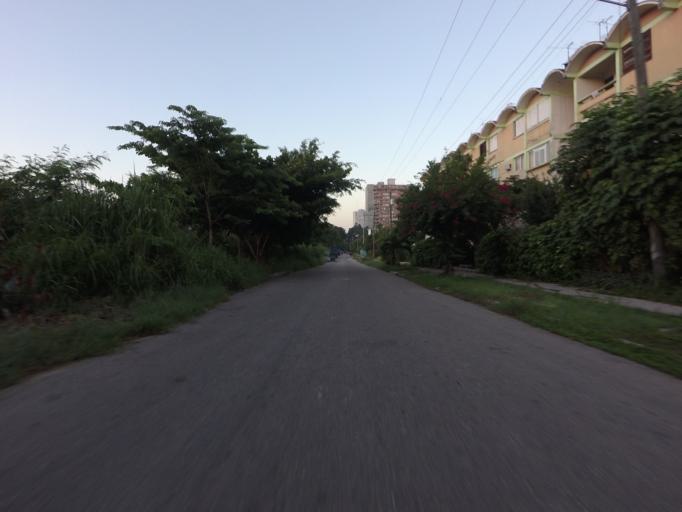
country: CU
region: La Habana
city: Havana
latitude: 23.1221
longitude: -82.3916
